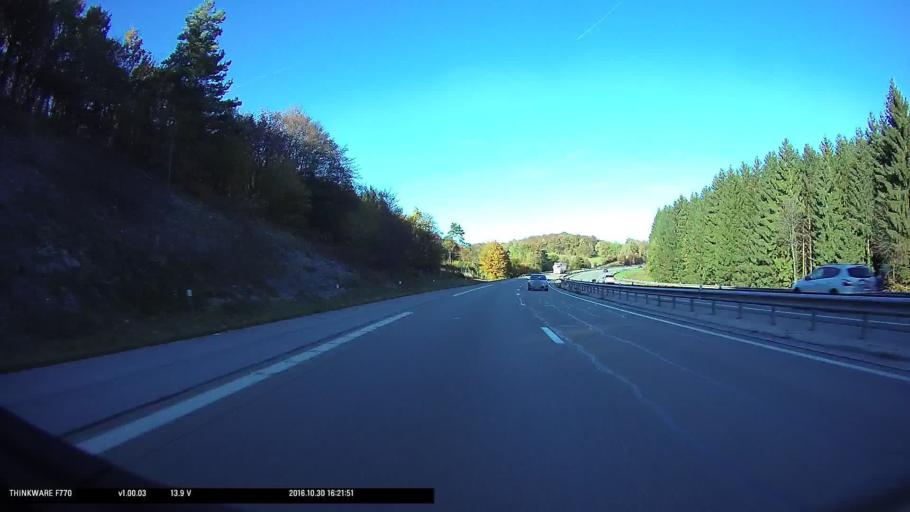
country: FR
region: Franche-Comte
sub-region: Departement du Doubs
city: Clerval
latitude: 47.3917
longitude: 6.4299
